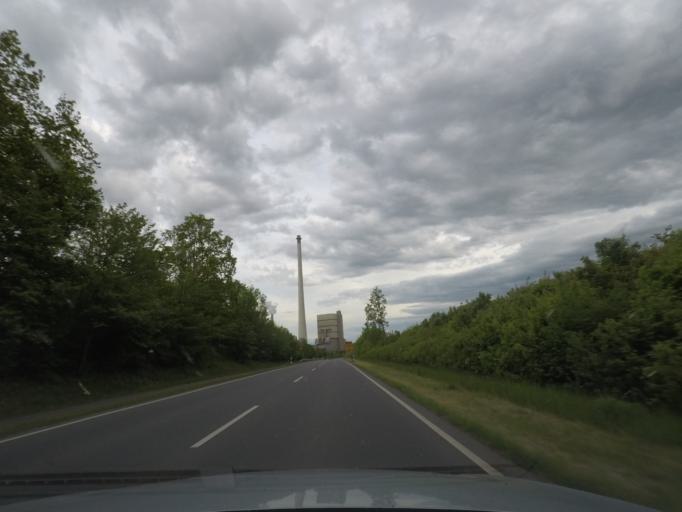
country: DE
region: Lower Saxony
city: Wolsdorf
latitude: 52.1793
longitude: 10.9758
